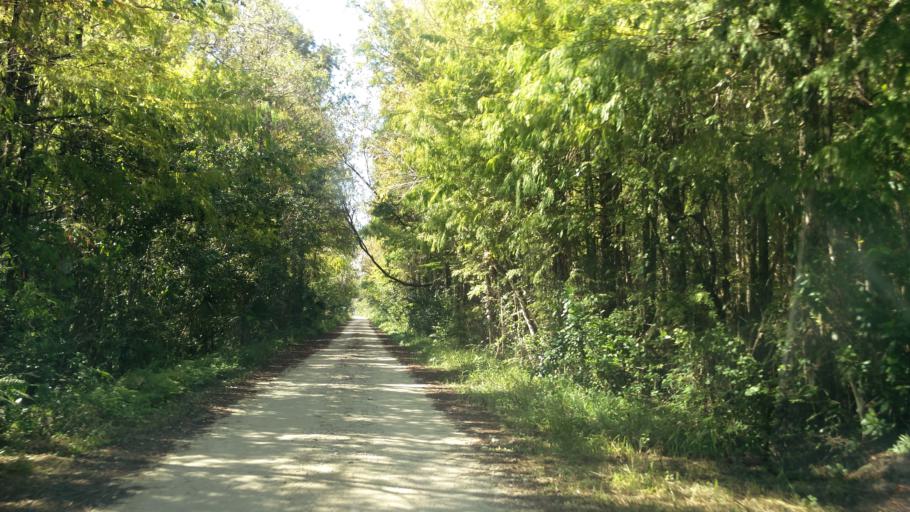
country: US
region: Florida
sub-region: Collier County
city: Lely Resort
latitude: 25.9800
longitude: -81.3983
